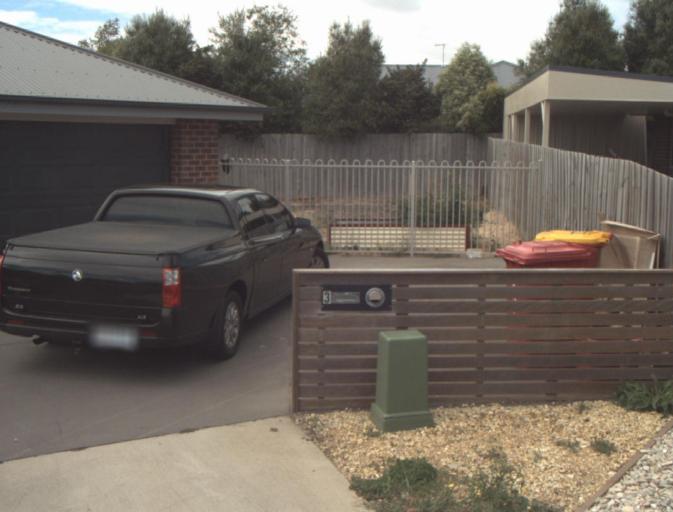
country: AU
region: Tasmania
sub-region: Launceston
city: Mayfield
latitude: -41.3888
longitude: 147.1156
